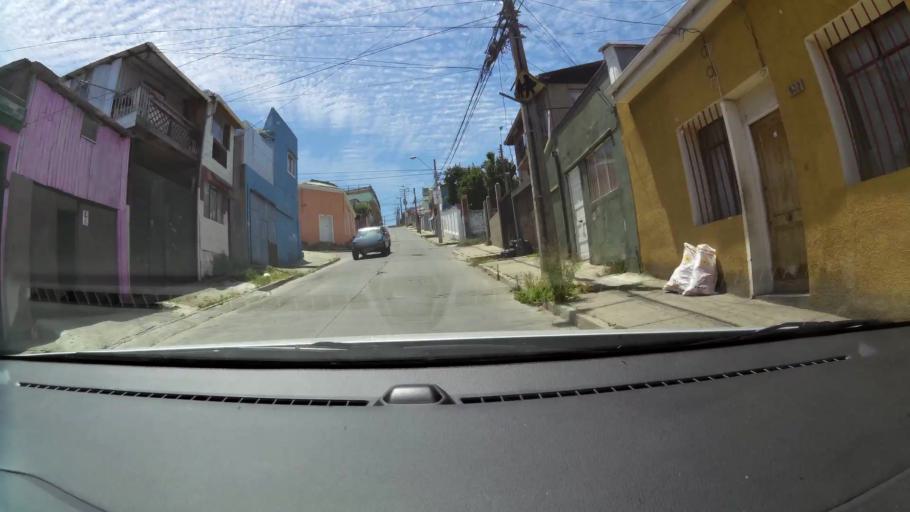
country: CL
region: Valparaiso
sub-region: Provincia de Valparaiso
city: Valparaiso
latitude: -33.0477
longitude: -71.5978
